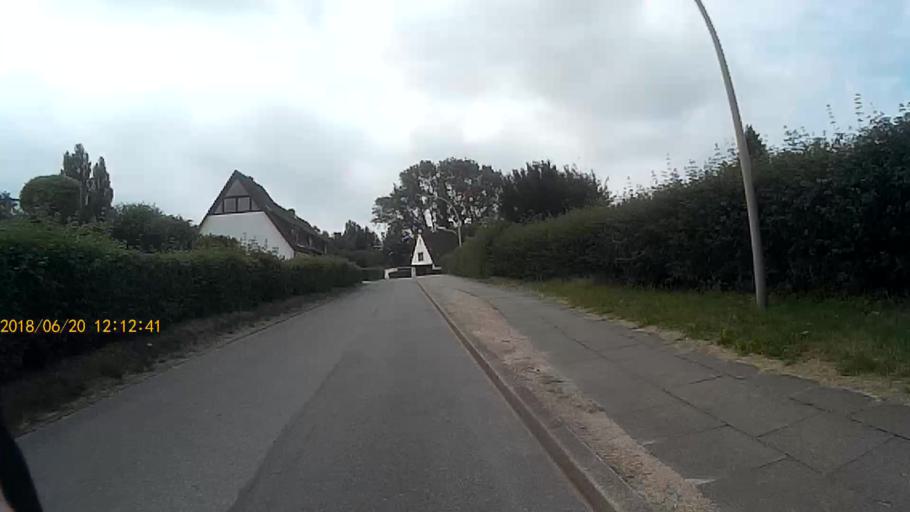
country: DE
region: Hamburg
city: Harburg
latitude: 53.4809
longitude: 10.0044
